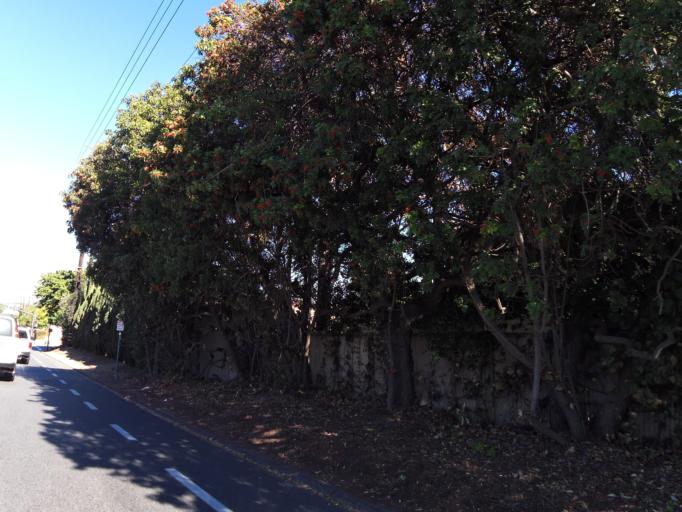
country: US
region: California
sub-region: Ventura County
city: Thousand Oaks
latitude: 34.2173
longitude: -118.8682
